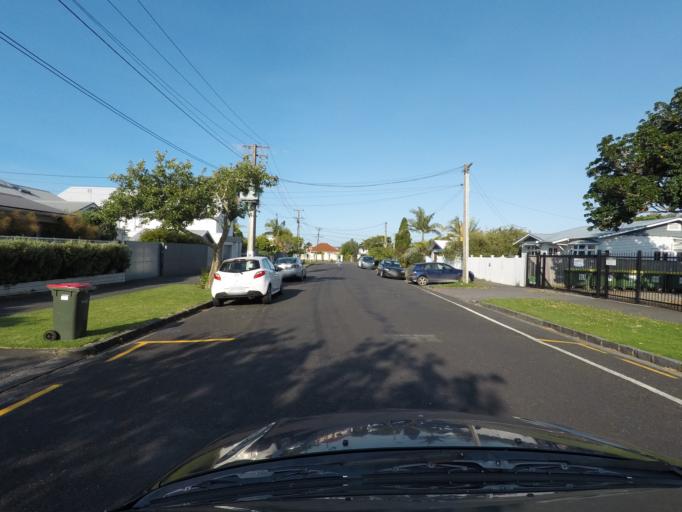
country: NZ
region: Auckland
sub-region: Auckland
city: Rosebank
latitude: -36.8598
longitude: 174.7051
